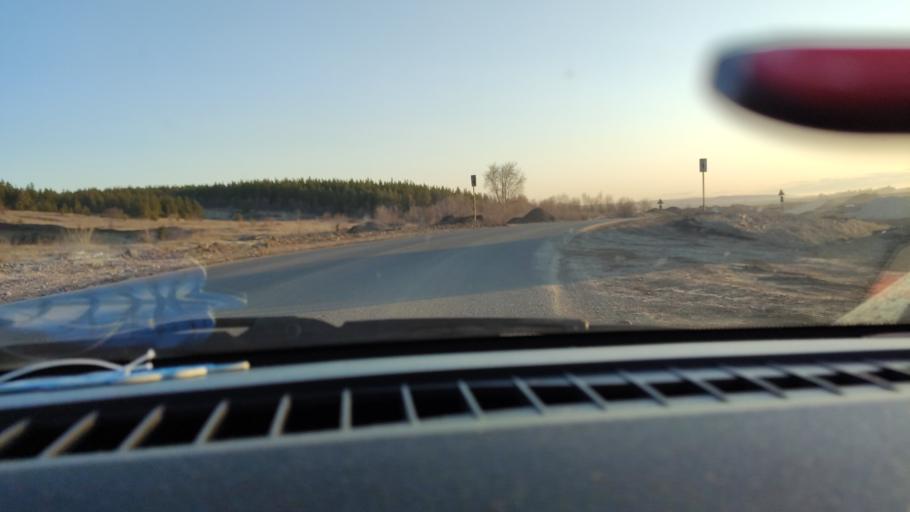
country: RU
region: Saratov
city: Sinodskoye
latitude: 52.0115
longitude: 46.6876
